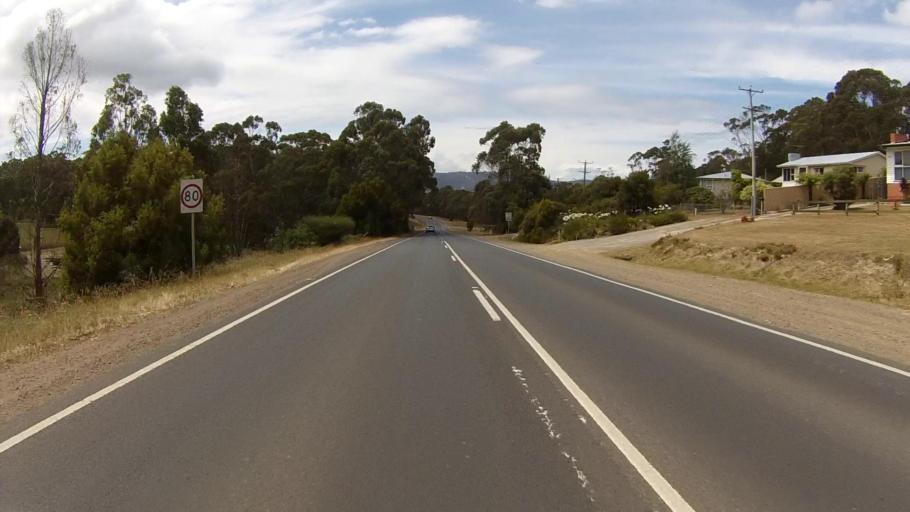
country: AU
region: Tasmania
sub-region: Kingborough
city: Margate
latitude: -43.0563
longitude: 147.2567
